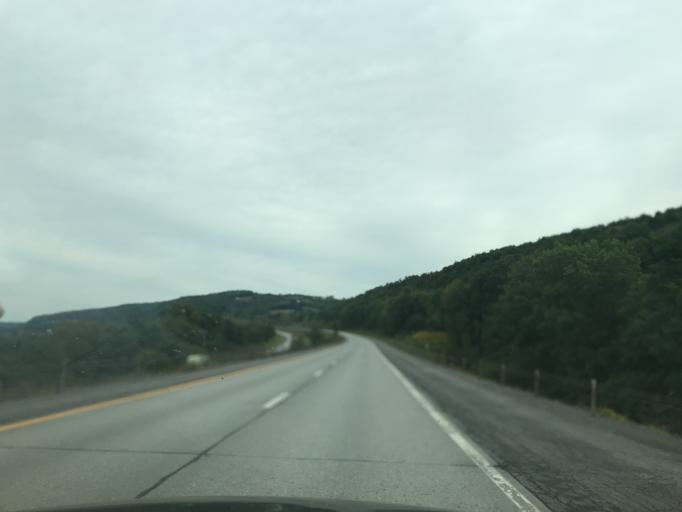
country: US
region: New York
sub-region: Schoharie County
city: Schoharie
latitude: 42.6797
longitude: -74.3872
